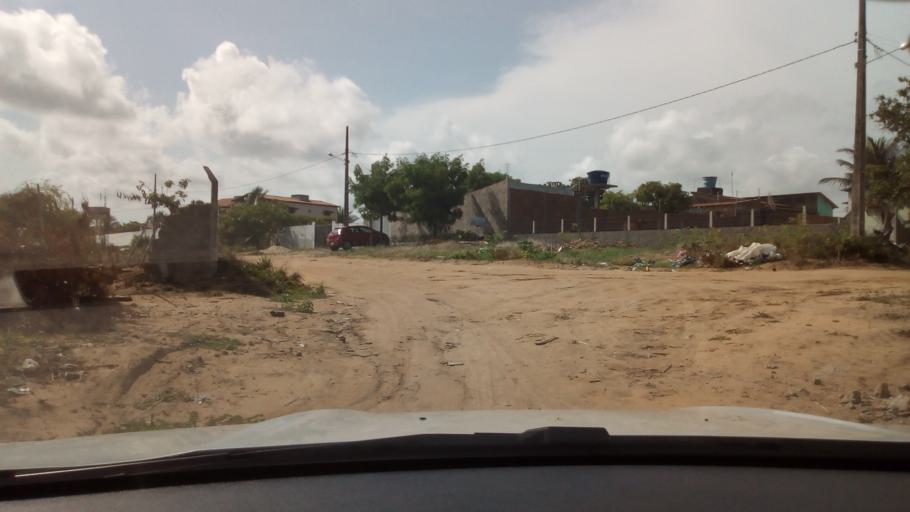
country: BR
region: Paraiba
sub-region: Conde
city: Conde
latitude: -7.3026
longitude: -34.8016
